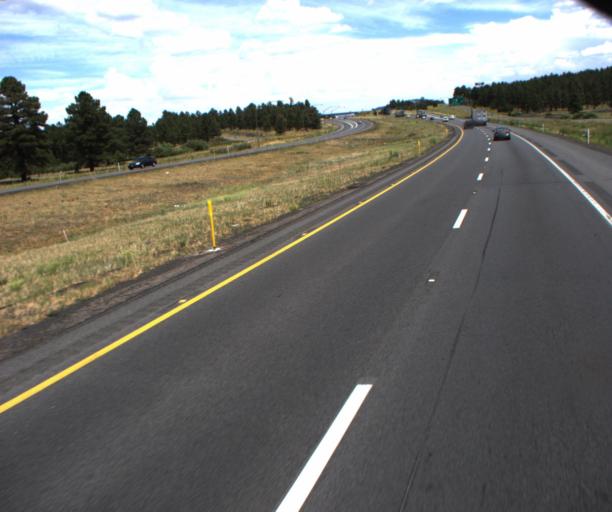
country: US
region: Arizona
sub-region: Coconino County
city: Williams
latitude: 35.2380
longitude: -112.2209
